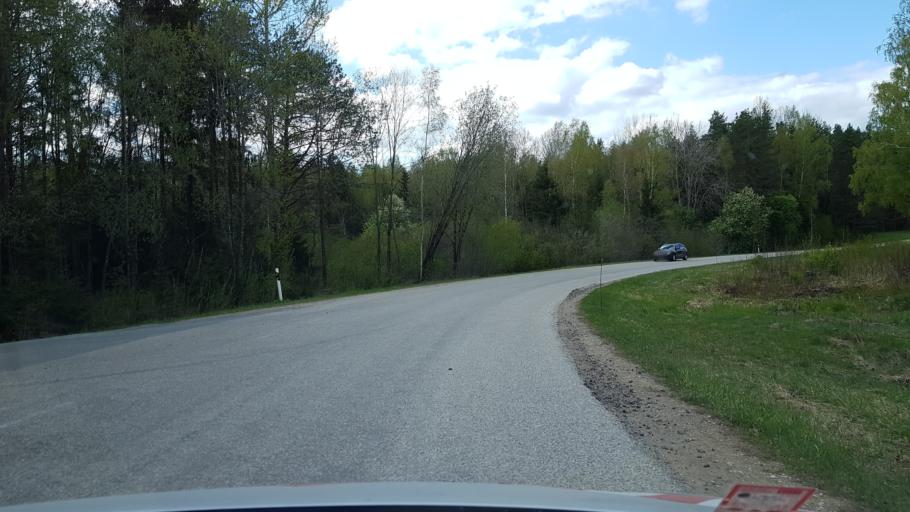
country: EE
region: Tartu
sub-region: Tartu linn
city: Tartu
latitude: 58.3487
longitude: 26.8059
